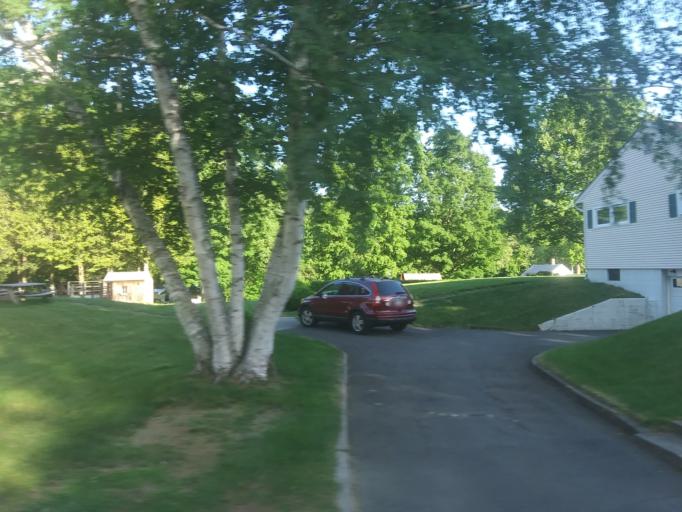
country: US
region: Massachusetts
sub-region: Franklin County
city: Shelburne Falls
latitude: 42.5961
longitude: -72.7385
